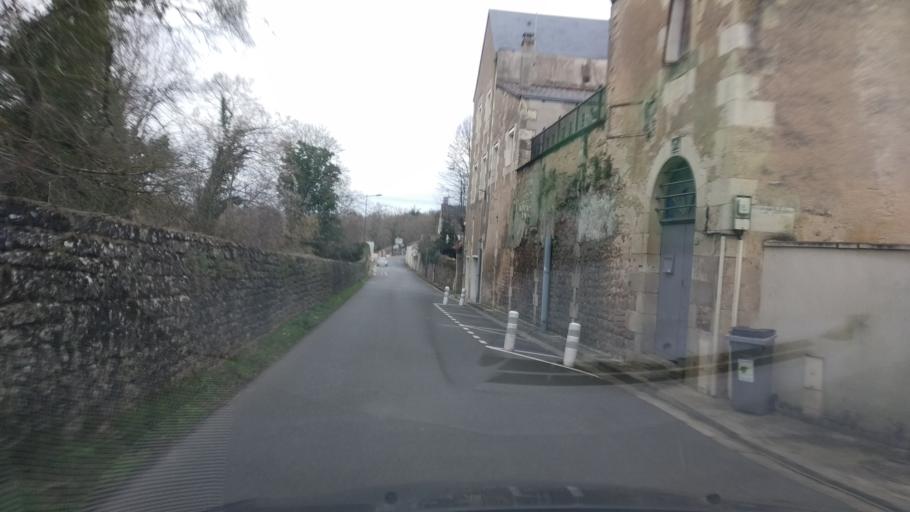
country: FR
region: Poitou-Charentes
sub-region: Departement de la Vienne
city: Dissay
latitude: 46.7019
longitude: 0.4319
